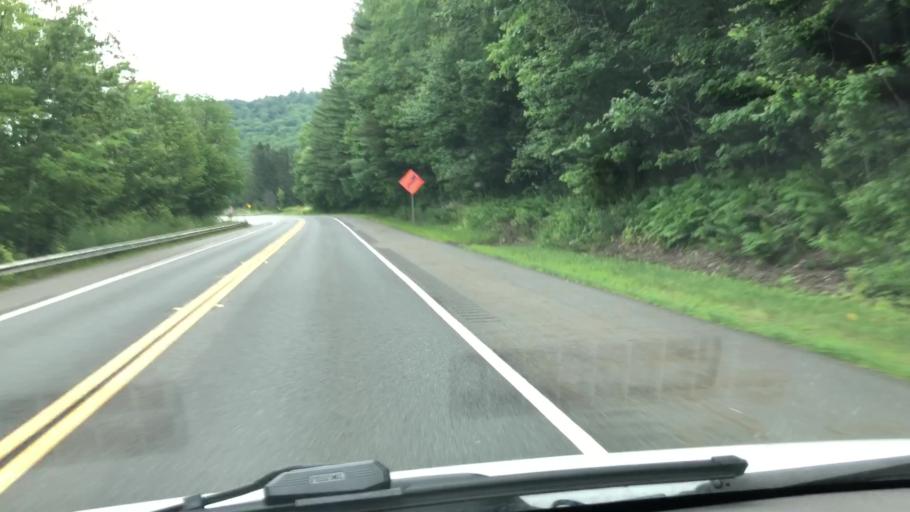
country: US
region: Massachusetts
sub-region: Hampshire County
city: Chesterfield
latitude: 42.4900
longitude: -72.9681
